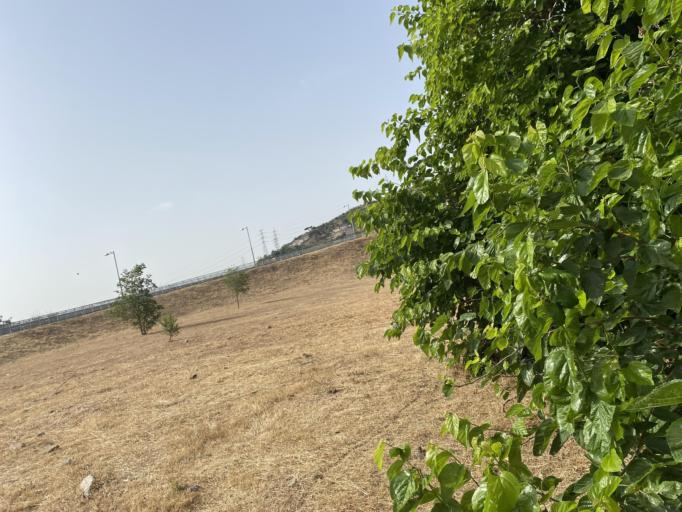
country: ES
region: Catalonia
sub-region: Provincia de Barcelona
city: Montcada i Reixac
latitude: 41.4626
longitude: 2.1844
